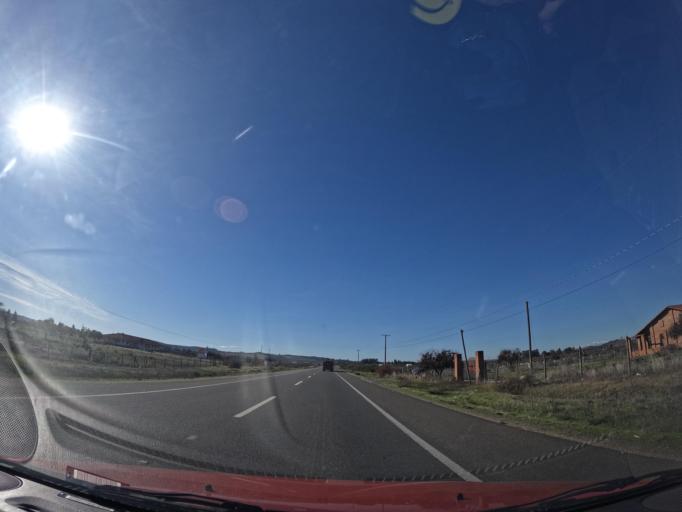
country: CL
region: Maule
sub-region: Provincia de Cauquenes
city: Cauquenes
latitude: -35.9548
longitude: -72.2110
